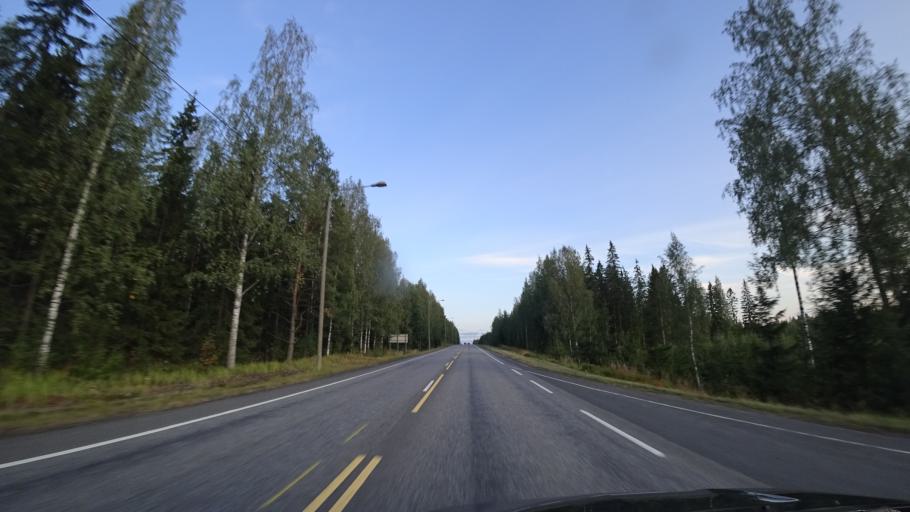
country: FI
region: Haeme
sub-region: Riihimaeki
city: Riihimaeki
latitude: 60.7485
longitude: 24.7258
